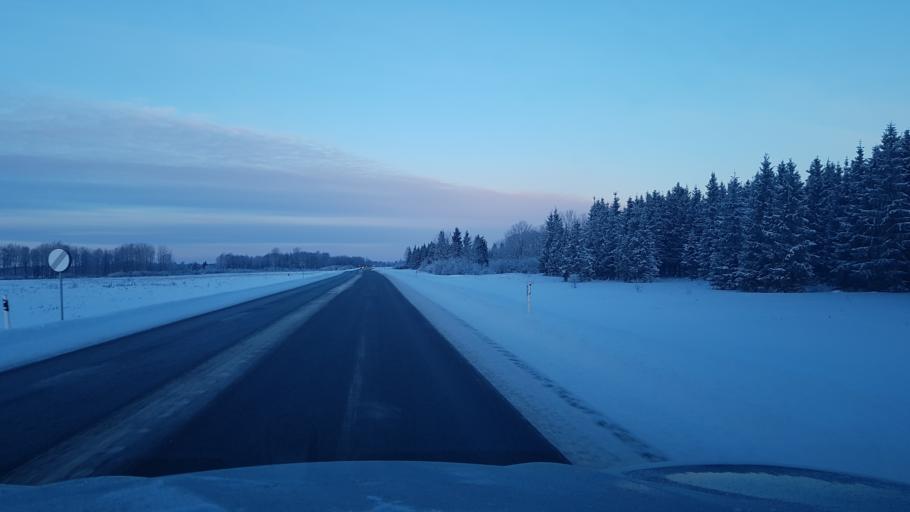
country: EE
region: Ida-Virumaa
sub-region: Narva-Joesuu linn
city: Narva-Joesuu
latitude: 59.3917
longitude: 28.0916
